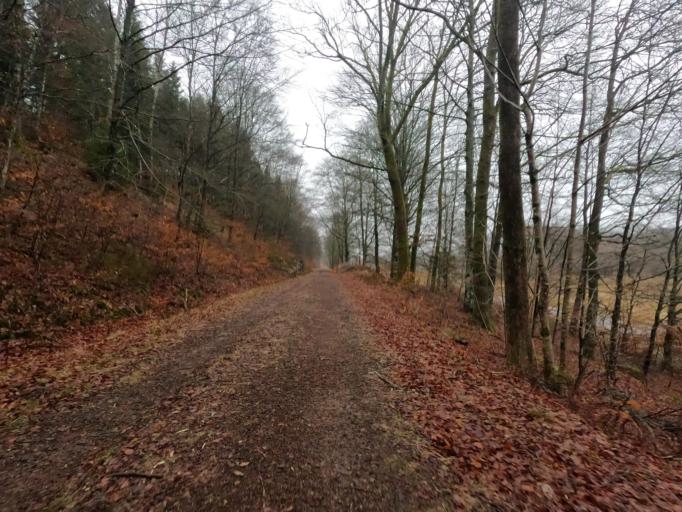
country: SE
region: Halland
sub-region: Halmstads Kommun
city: Oskarstrom
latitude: 56.7433
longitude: 13.1652
